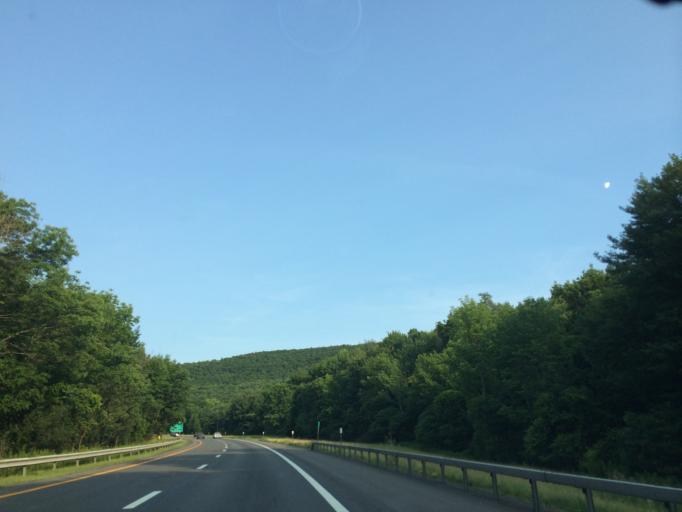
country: US
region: Massachusetts
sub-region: Berkshire County
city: Richmond
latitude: 42.3686
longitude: -73.4573
